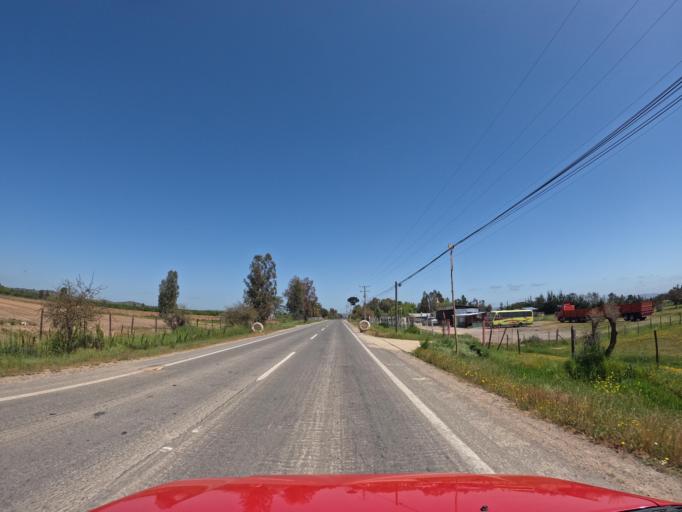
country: CL
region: O'Higgins
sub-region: Provincia de Colchagua
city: Santa Cruz
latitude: -34.7336
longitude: -71.6880
